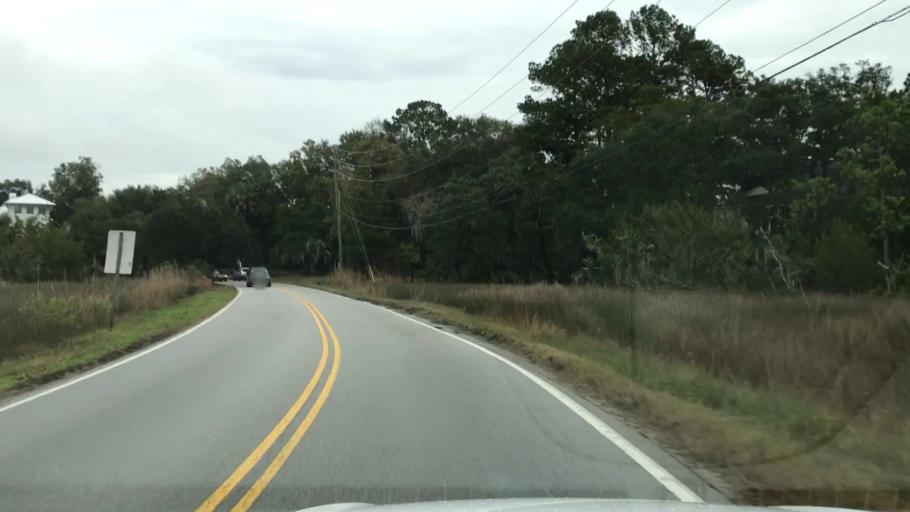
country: US
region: South Carolina
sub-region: Charleston County
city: Mount Pleasant
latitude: 32.8451
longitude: -79.8301
